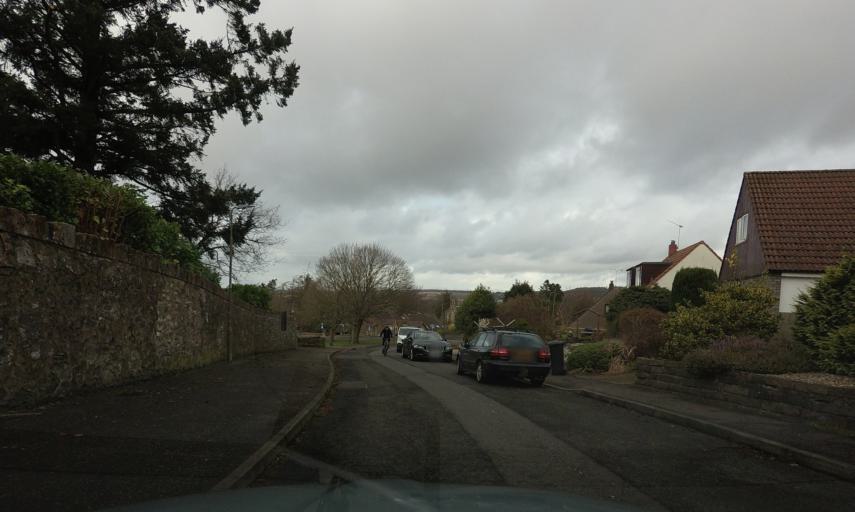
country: GB
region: Scotland
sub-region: West Lothian
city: Linlithgow
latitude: 55.9708
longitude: -3.6021
